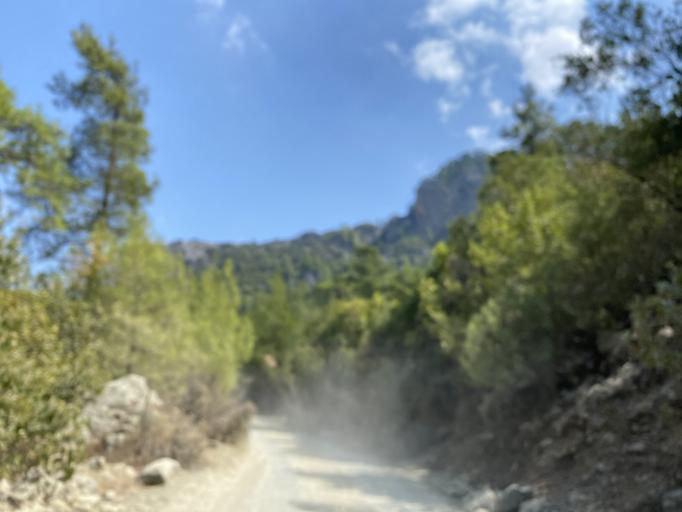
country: TR
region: Antalya
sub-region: Kemer
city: Goeynuek
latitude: 36.6807
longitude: 30.5232
